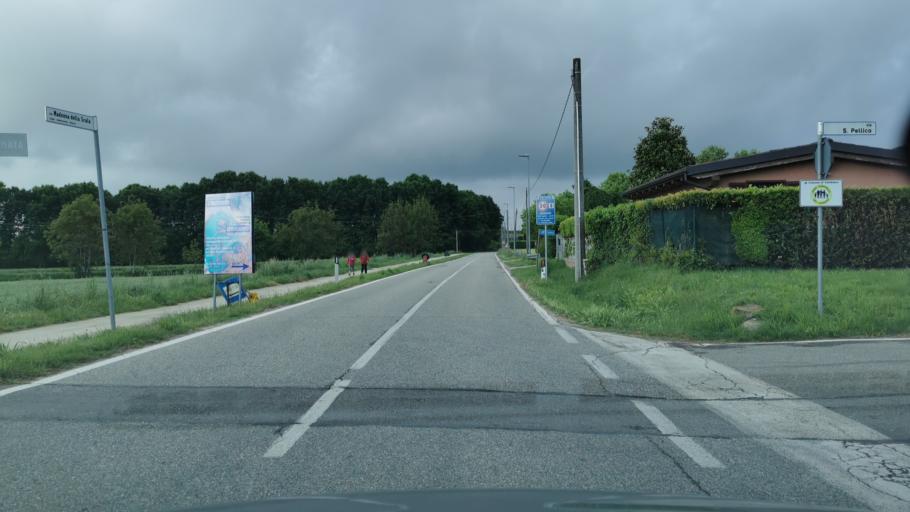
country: IT
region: Piedmont
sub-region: Provincia di Torino
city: Cambiano
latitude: 44.9965
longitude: 7.7836
